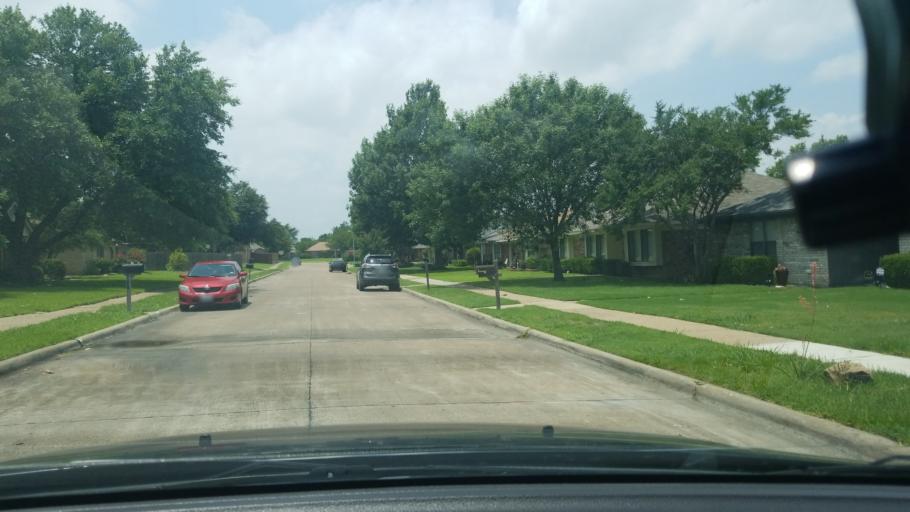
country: US
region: Texas
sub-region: Dallas County
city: Mesquite
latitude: 32.7996
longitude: -96.6133
